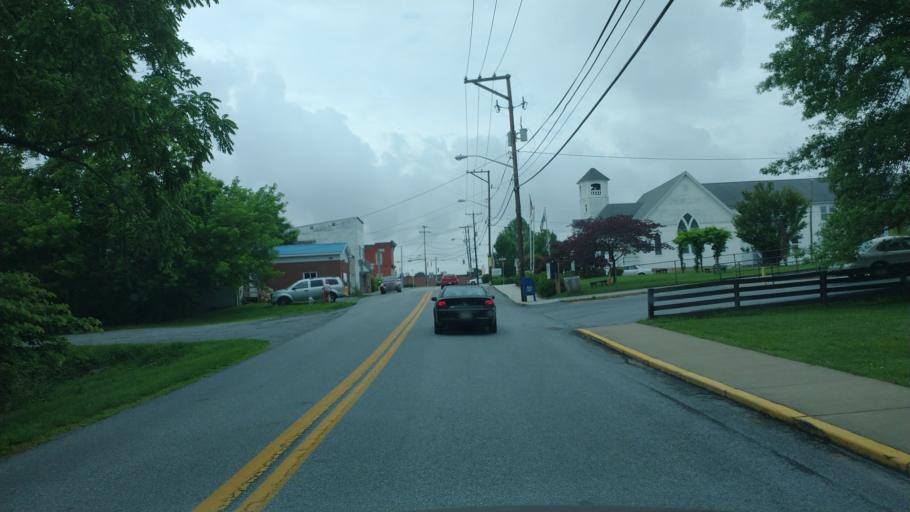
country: US
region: West Virginia
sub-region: Mercer County
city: Athens
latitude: 37.4233
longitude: -81.0142
